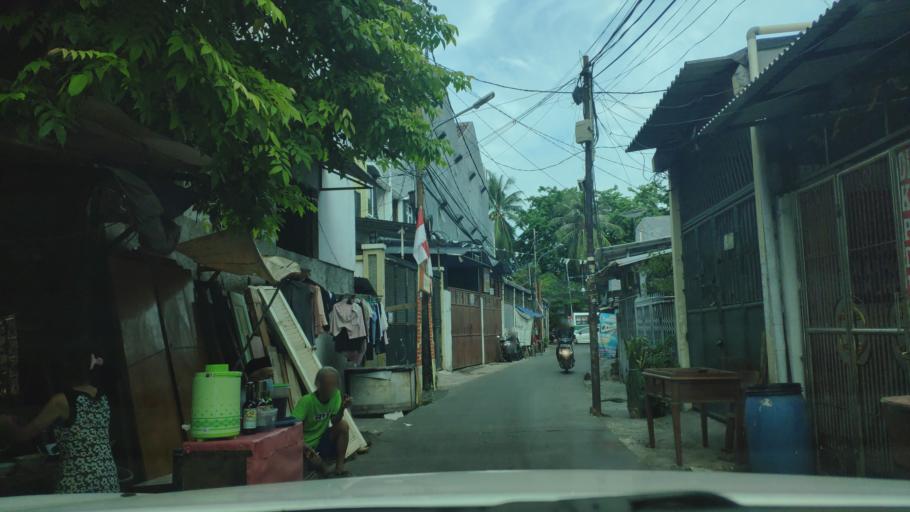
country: ID
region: Jakarta Raya
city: Jakarta
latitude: -6.1468
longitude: 106.8200
